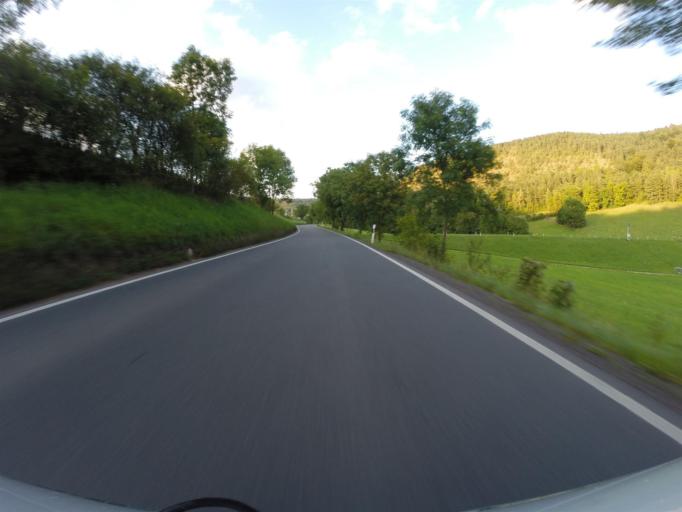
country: DE
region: Thuringia
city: Bucha
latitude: 50.8955
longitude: 11.5483
